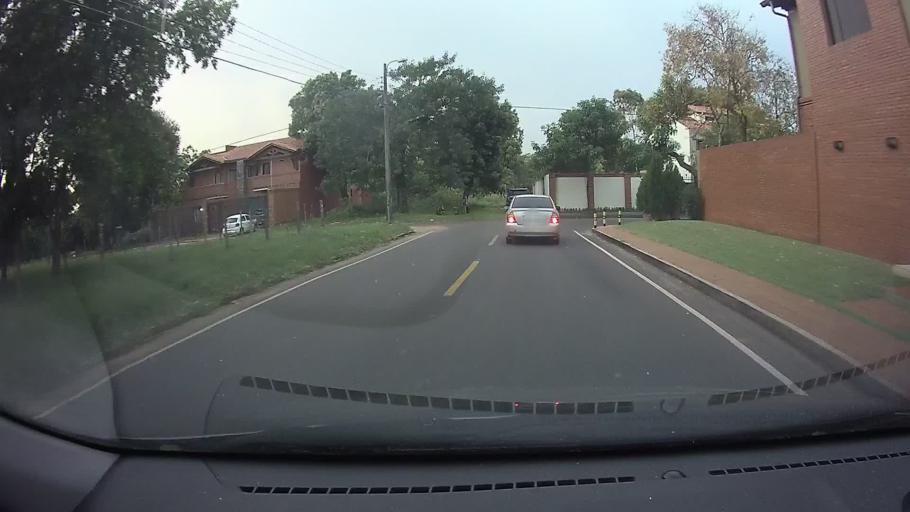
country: PY
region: Central
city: San Lorenzo
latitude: -25.2557
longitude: -57.5033
